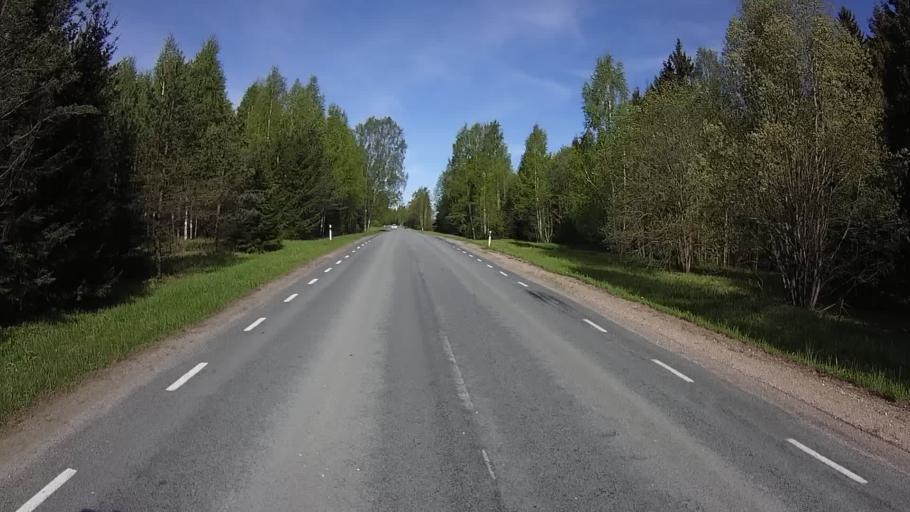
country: EE
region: Polvamaa
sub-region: Polva linn
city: Polva
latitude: 58.2214
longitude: 27.0548
